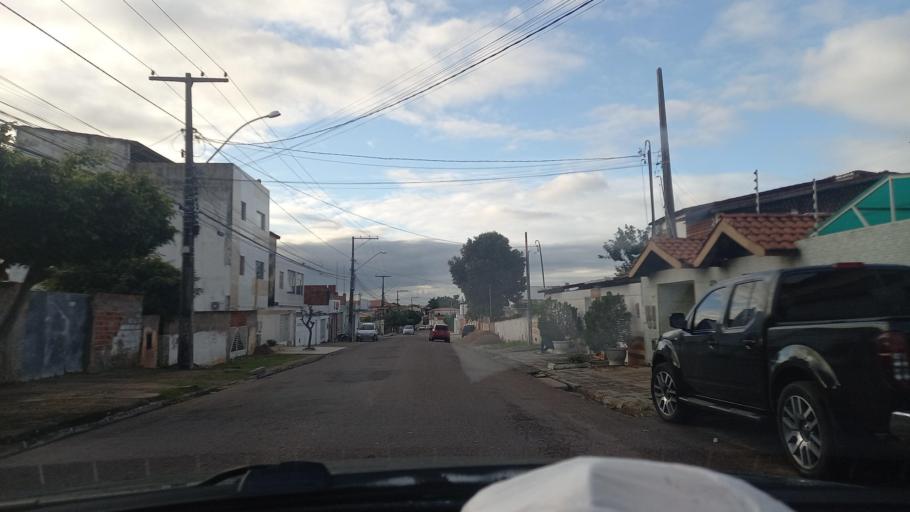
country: BR
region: Bahia
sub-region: Paulo Afonso
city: Paulo Afonso
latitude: -9.3977
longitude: -38.2374
